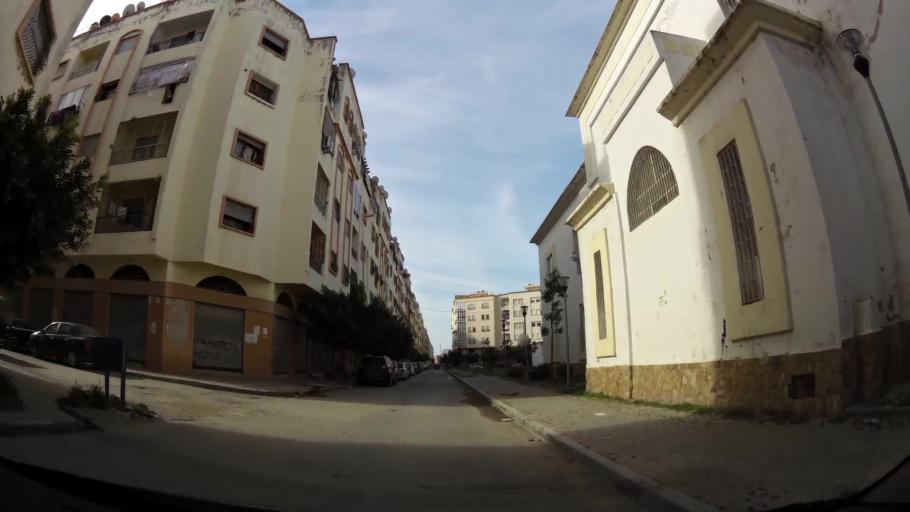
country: MA
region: Tanger-Tetouan
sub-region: Tanger-Assilah
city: Tangier
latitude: 35.7414
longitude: -5.7979
